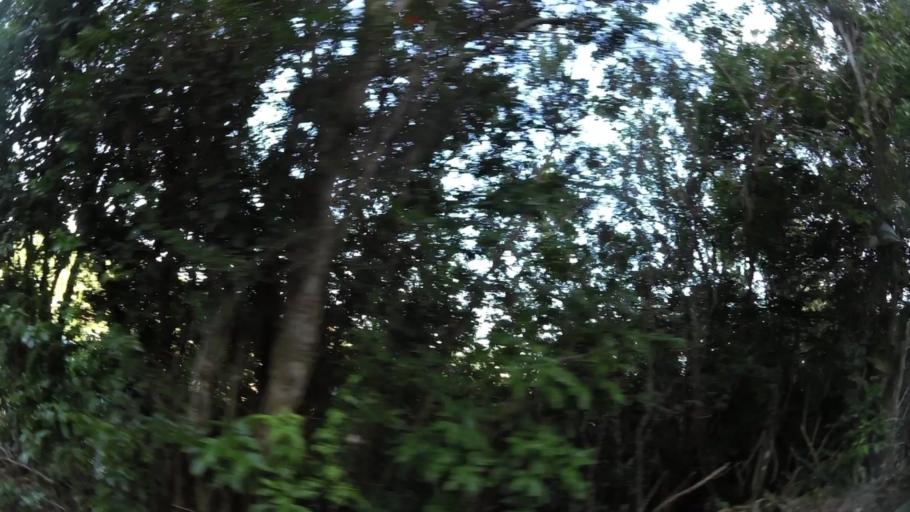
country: VG
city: Road Town
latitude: 18.4362
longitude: -64.6358
